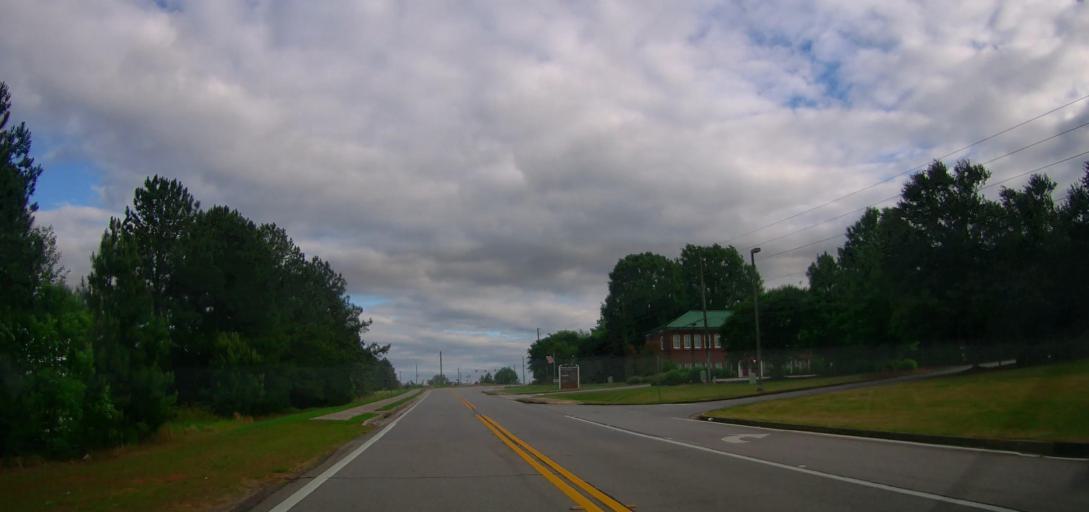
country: US
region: Georgia
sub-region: Oconee County
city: Watkinsville
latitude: 33.9191
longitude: -83.4619
